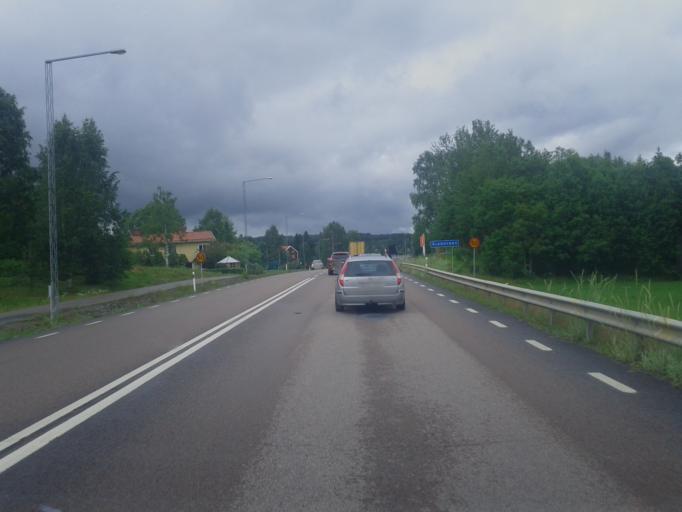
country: SE
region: Vaesternorrland
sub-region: Haernoesands Kommun
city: Haernoesand
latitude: 62.6696
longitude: 17.8407
